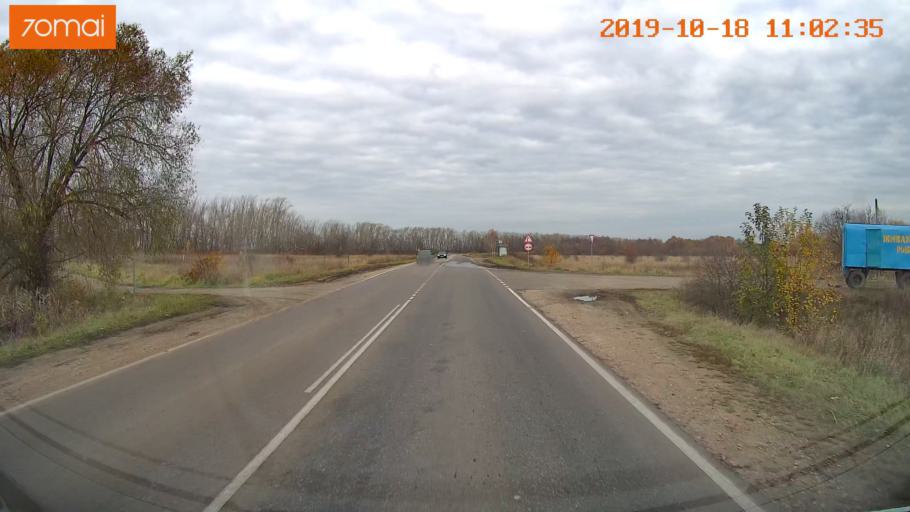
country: RU
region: Tula
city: Yepifan'
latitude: 53.8678
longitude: 38.5440
